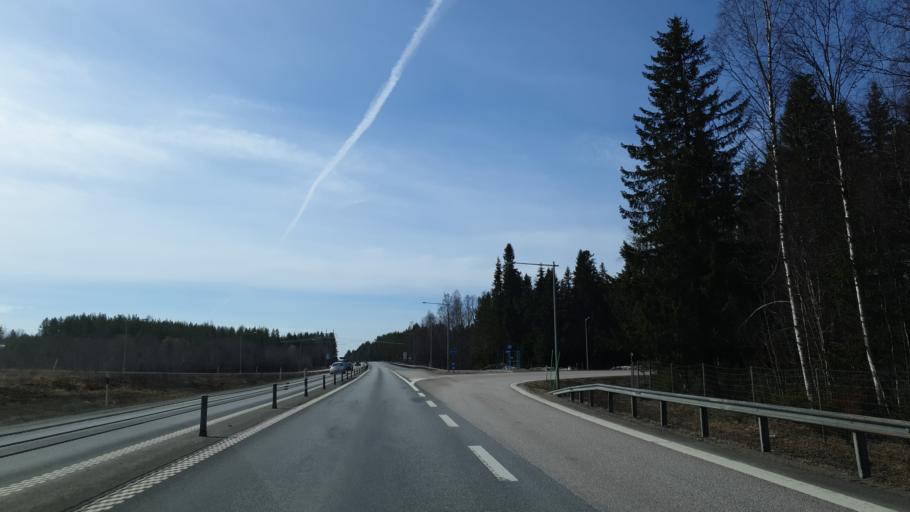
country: SE
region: Vaesterbotten
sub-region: Nordmalings Kommun
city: Nordmaling
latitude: 63.5490
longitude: 19.4135
